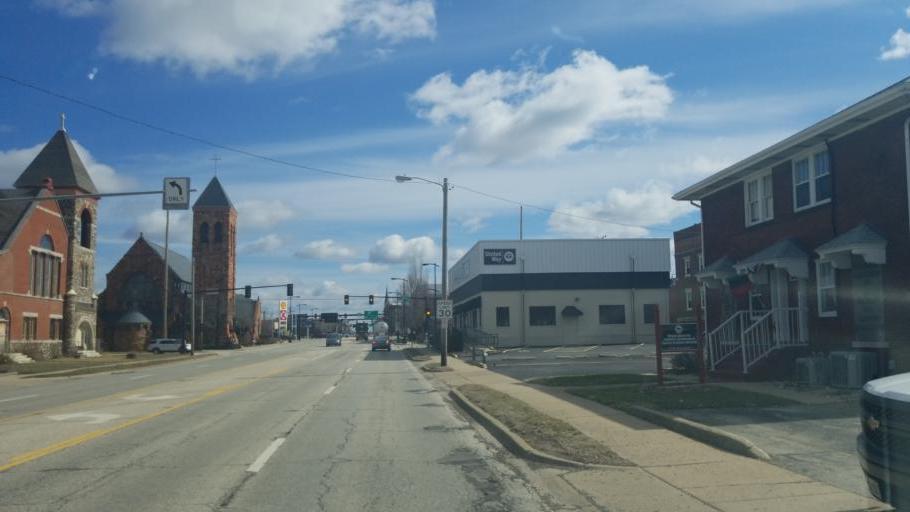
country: US
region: Illinois
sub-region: Macon County
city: Decatur
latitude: 39.8457
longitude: -88.9584
